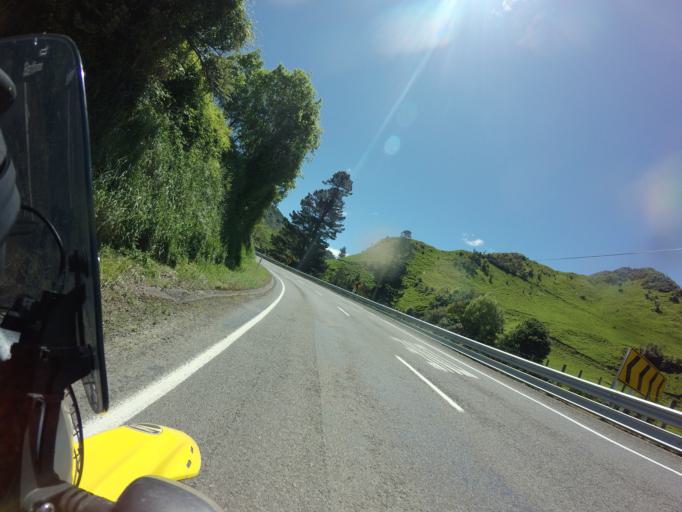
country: NZ
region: Bay of Plenty
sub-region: Opotiki District
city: Opotiki
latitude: -38.3777
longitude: 177.4690
